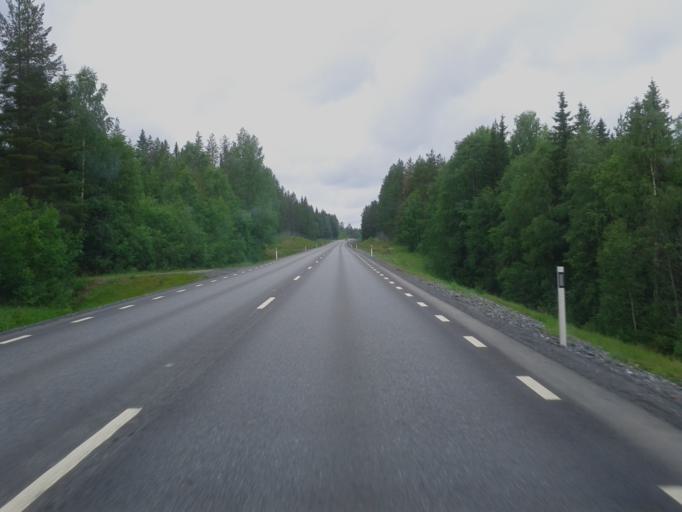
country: SE
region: Vaesterbotten
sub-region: Skelleftea Kommun
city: Boliden
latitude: 64.8580
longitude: 20.4698
